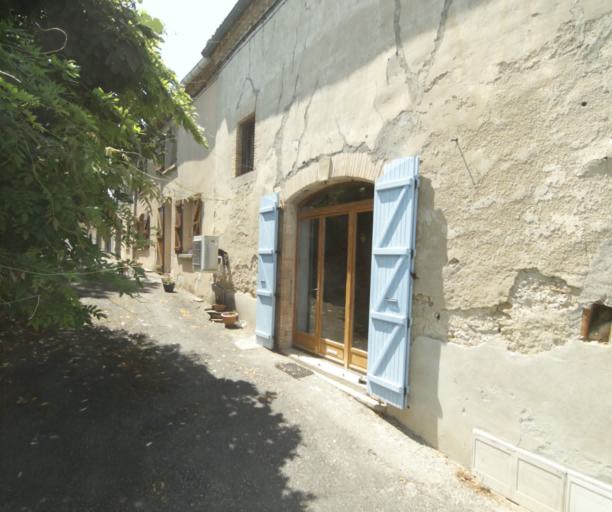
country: FR
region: Midi-Pyrenees
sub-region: Departement de la Haute-Garonne
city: Saint-Felix-Lauragais
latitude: 43.4569
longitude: 1.8364
